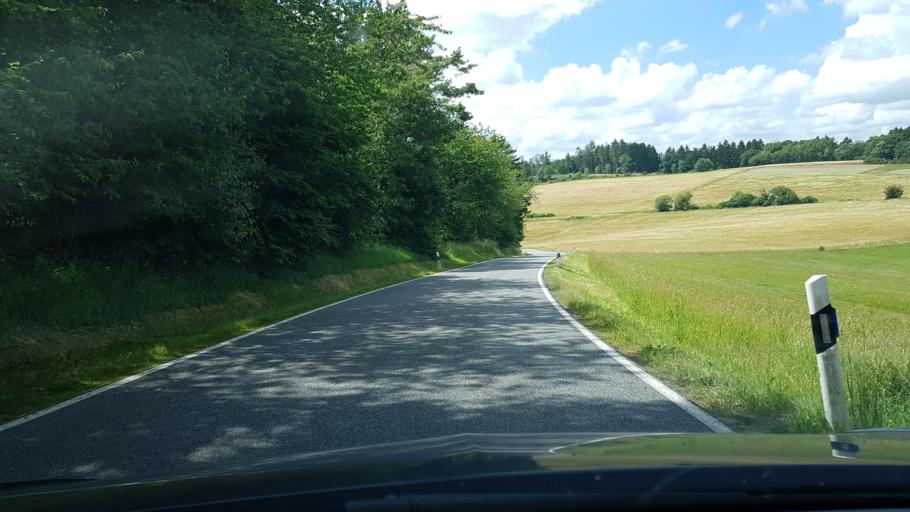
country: DE
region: Rheinland-Pfalz
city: Siebenbach
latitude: 50.3934
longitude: 7.0487
